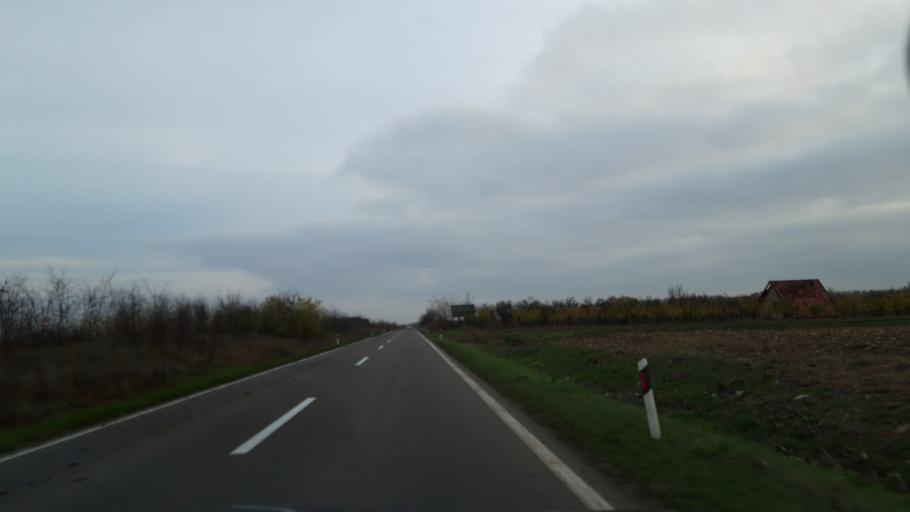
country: RS
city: Sanad
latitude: 45.9955
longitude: 20.1053
